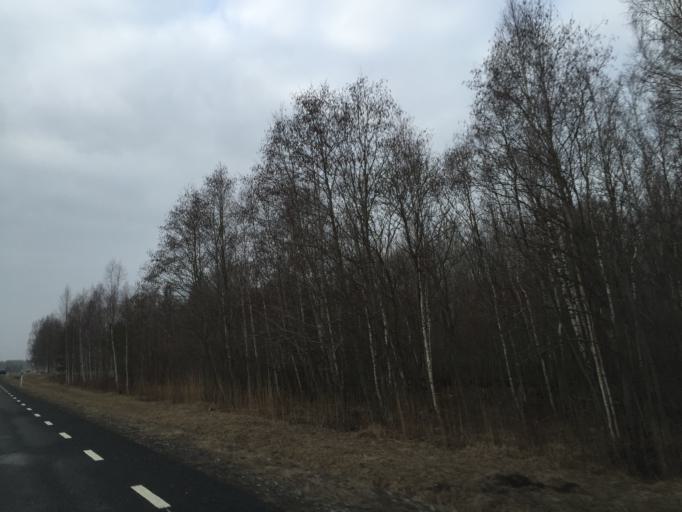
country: EE
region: Saare
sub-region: Orissaare vald
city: Orissaare
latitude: 58.5818
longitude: 23.3553
